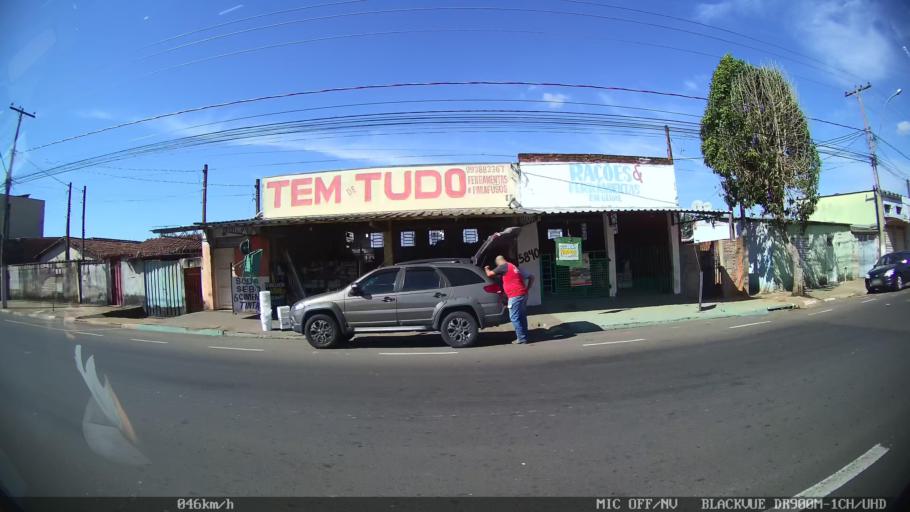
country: BR
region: Sao Paulo
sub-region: Franca
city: Franca
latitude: -20.4999
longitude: -47.3982
